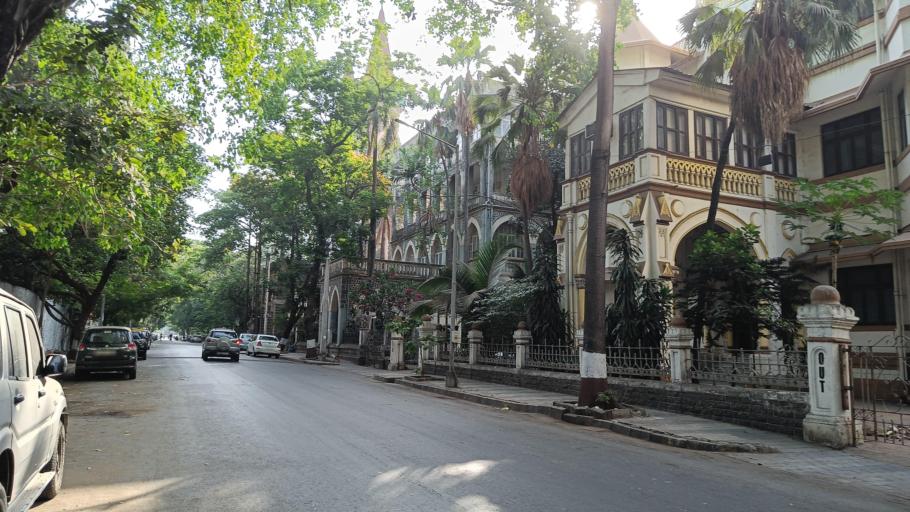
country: IN
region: Maharashtra
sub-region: Raigarh
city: Uran
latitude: 18.9233
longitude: 72.8299
